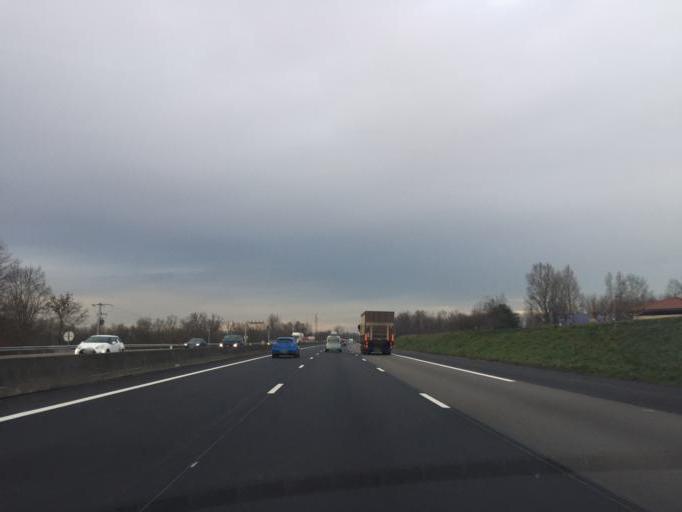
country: FR
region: Rhone-Alpes
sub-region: Departement du Rhone
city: Saint-Georges-de-Reneins
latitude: 46.0429
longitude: 4.7279
